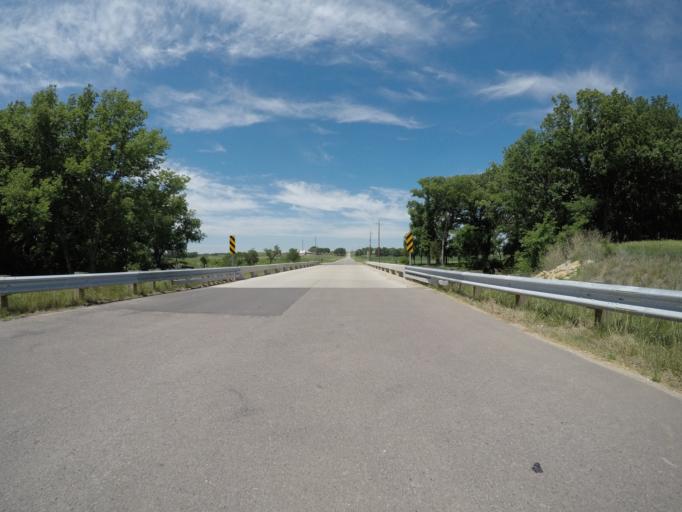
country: US
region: Kansas
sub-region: Wabaunsee County
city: Alma
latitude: 39.0360
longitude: -96.2689
